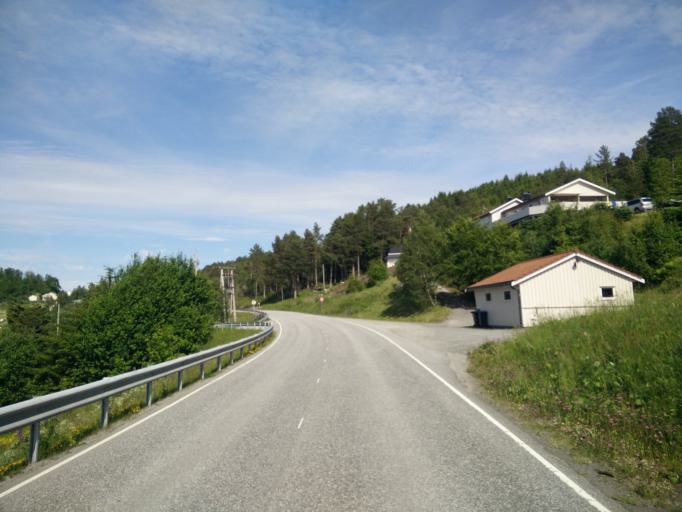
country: NO
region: More og Romsdal
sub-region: Kristiansund
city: Rensvik
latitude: 63.0175
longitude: 8.0067
